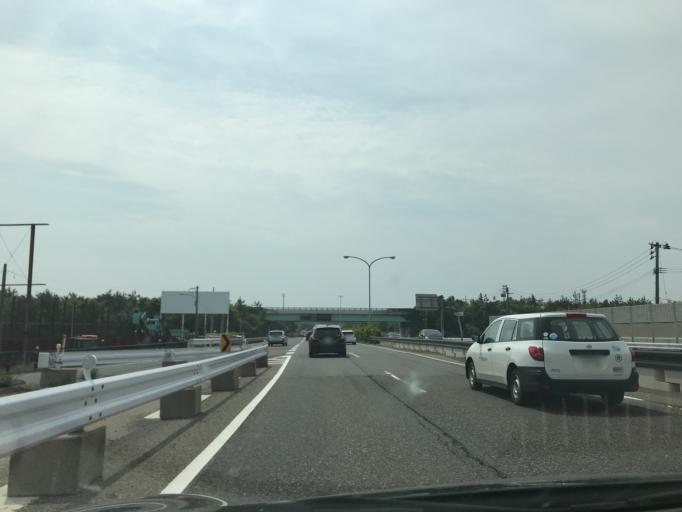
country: JP
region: Niigata
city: Kameda-honcho
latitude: 37.8825
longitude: 139.0805
